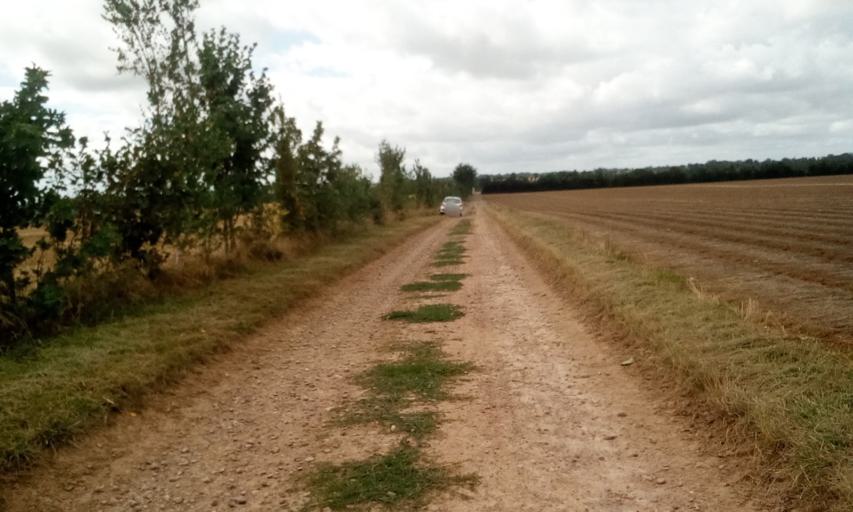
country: FR
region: Lower Normandy
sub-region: Departement du Calvados
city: Tilly-sur-Seulles
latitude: 49.2040
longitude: -0.6184
